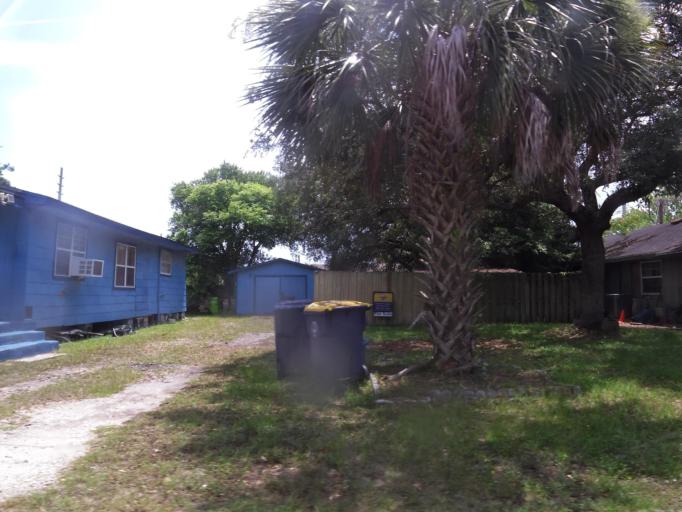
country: US
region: Florida
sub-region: Nassau County
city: Fernandina Beach
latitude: 30.6570
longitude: -81.4592
